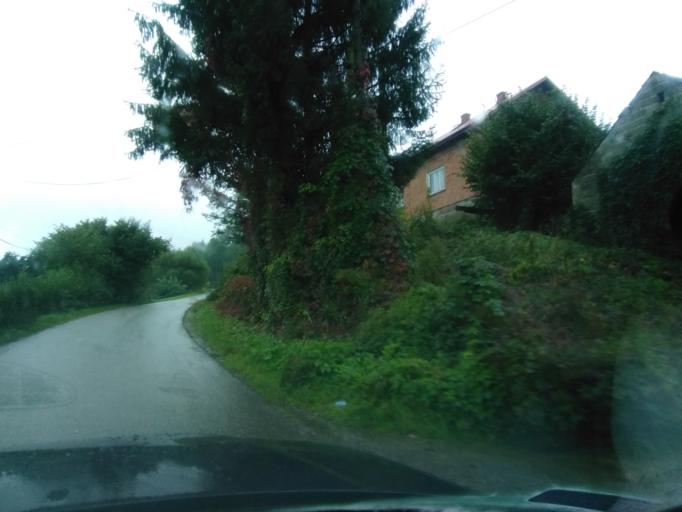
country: PL
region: Subcarpathian Voivodeship
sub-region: Powiat ropczycko-sedziszowski
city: Niedzwiada
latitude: 50.0119
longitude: 21.5478
